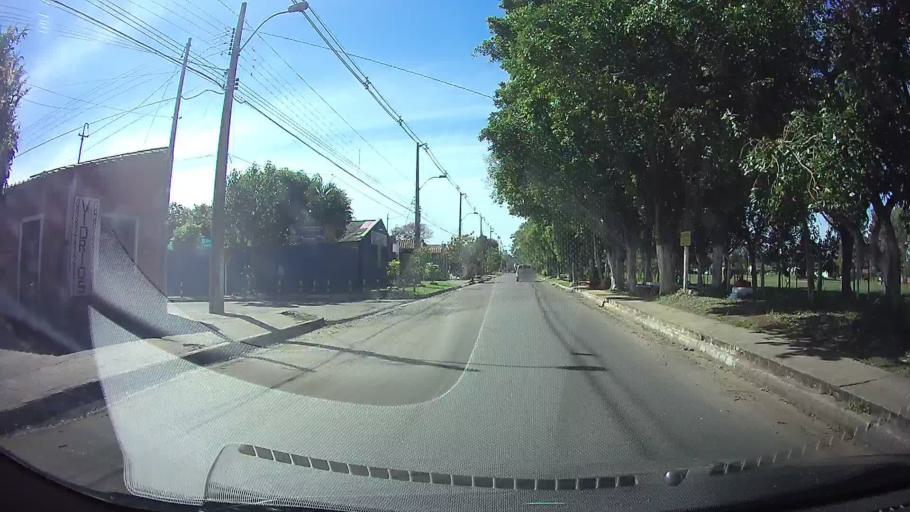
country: PY
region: Central
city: Colonia Mariano Roque Alonso
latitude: -25.2455
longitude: -57.5461
